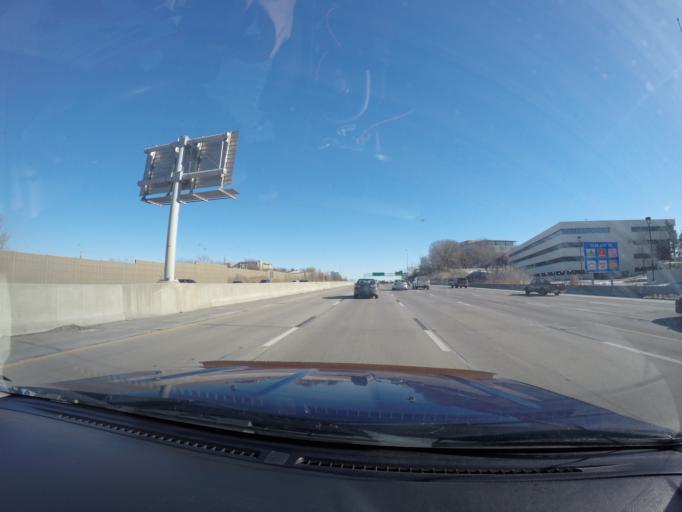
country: US
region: Kansas
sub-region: Johnson County
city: Overland Park
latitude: 38.9336
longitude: -94.6759
